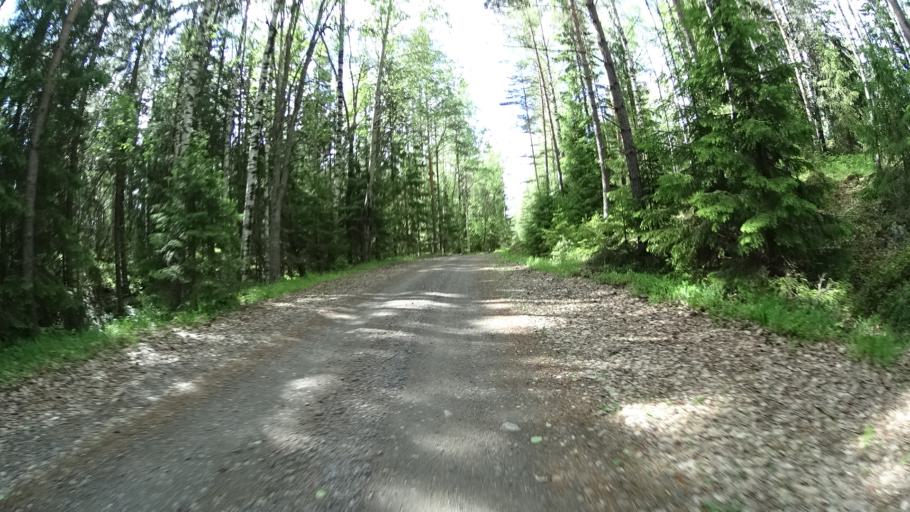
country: FI
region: Uusimaa
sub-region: Raaseporin
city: Pohja
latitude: 60.1780
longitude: 23.5467
